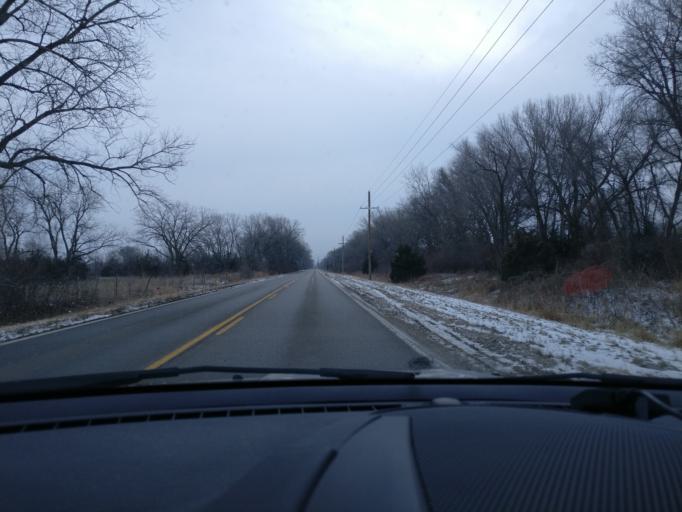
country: US
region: Nebraska
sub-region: Dodge County
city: Fremont
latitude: 41.4458
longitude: -96.5455
